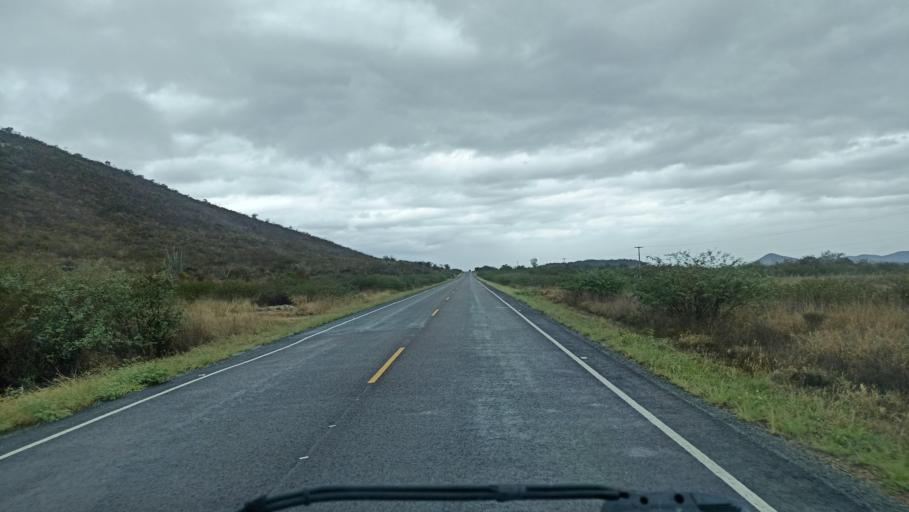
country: BR
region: Bahia
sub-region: Iacu
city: Iacu
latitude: -12.9571
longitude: -40.4700
